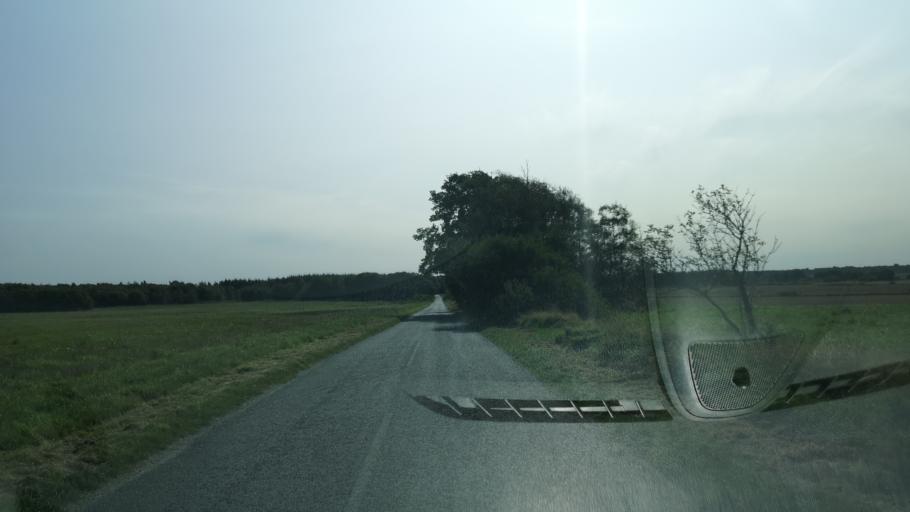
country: DK
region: Central Jutland
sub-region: Herning Kommune
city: Herning
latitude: 56.1743
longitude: 8.9532
